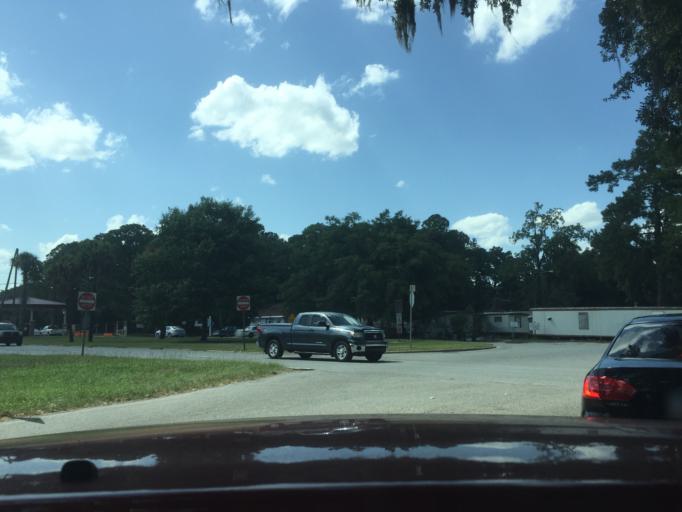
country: US
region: Georgia
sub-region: Chatham County
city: Savannah
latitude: 32.0276
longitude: -81.1201
